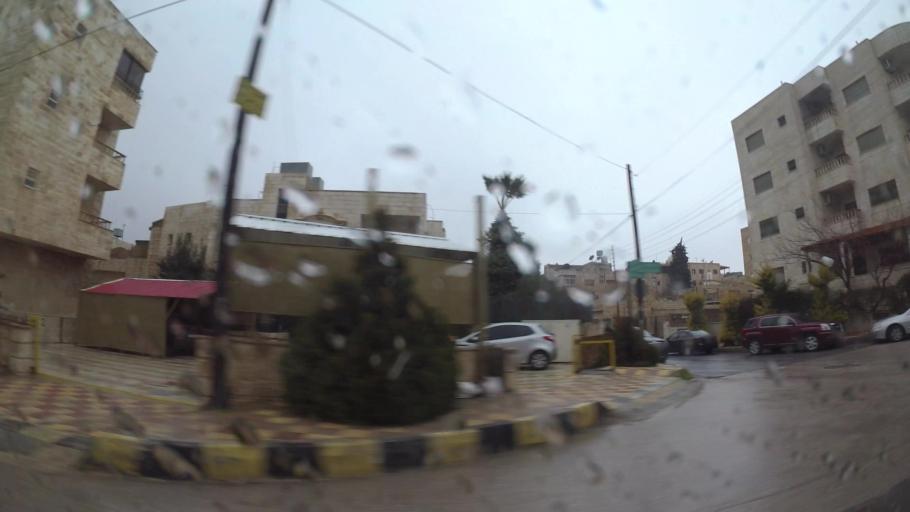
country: JO
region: Amman
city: Al Jubayhah
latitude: 32.0277
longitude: 35.8534
